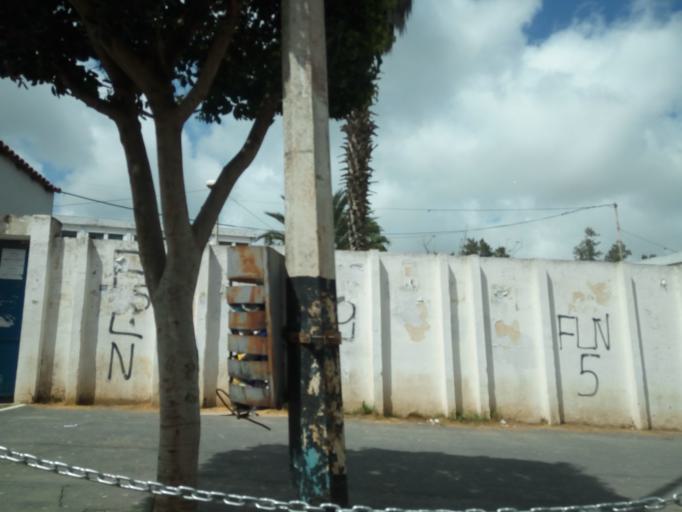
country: DZ
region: Tipaza
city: Douera
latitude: 36.6991
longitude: 2.9765
